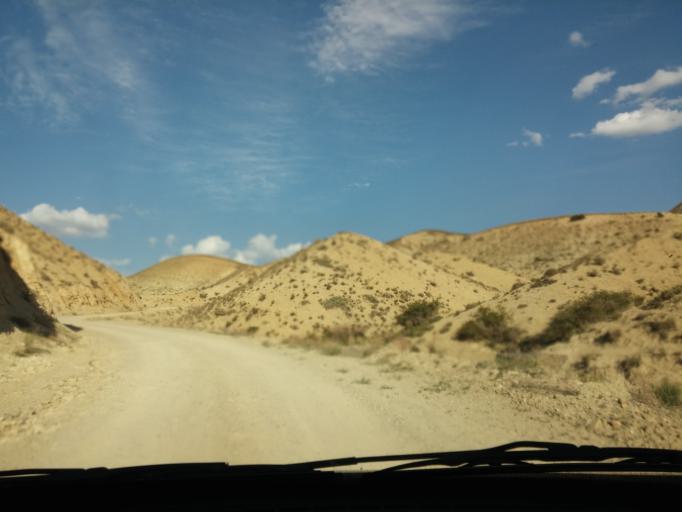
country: IR
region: Tehran
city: Damavand
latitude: 35.5348
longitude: 52.1991
